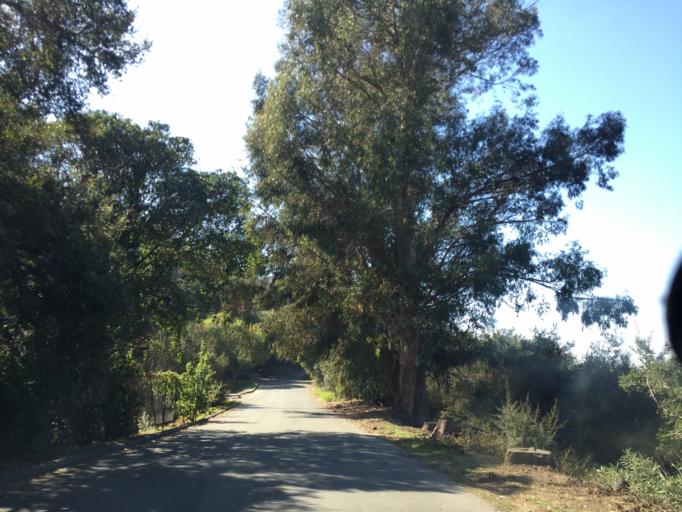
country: US
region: California
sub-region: Santa Barbara County
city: Goleta
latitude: 34.4332
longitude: -119.7742
